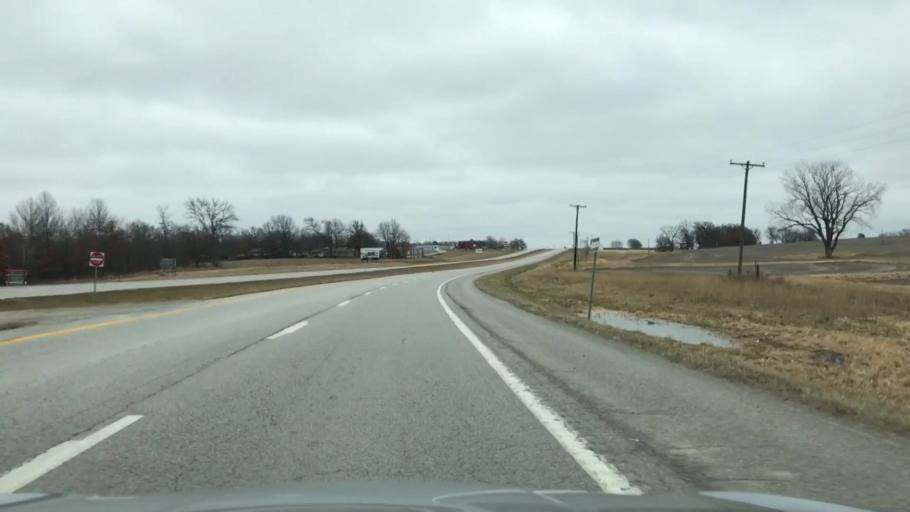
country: US
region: Missouri
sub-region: Livingston County
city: Chillicothe
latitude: 39.7751
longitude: -93.5297
